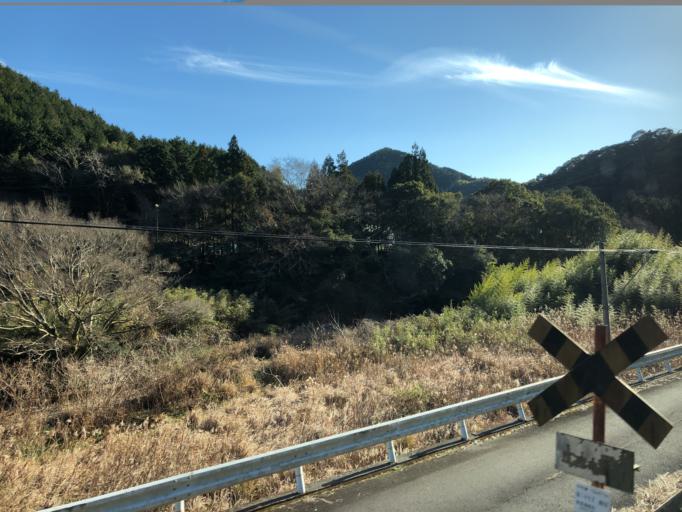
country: JP
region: Kochi
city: Nakamura
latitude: 33.1200
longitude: 133.1168
